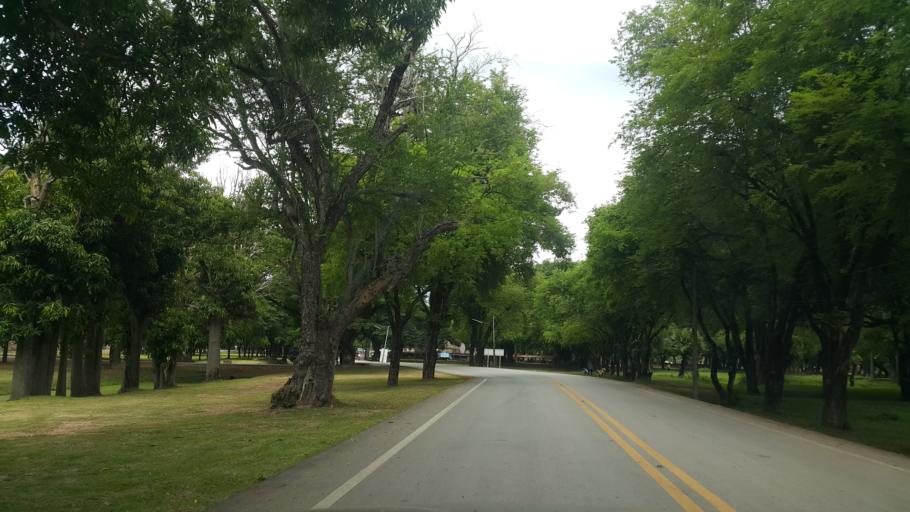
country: TH
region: Sukhothai
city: Ban Na
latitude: 17.0244
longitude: 99.7035
